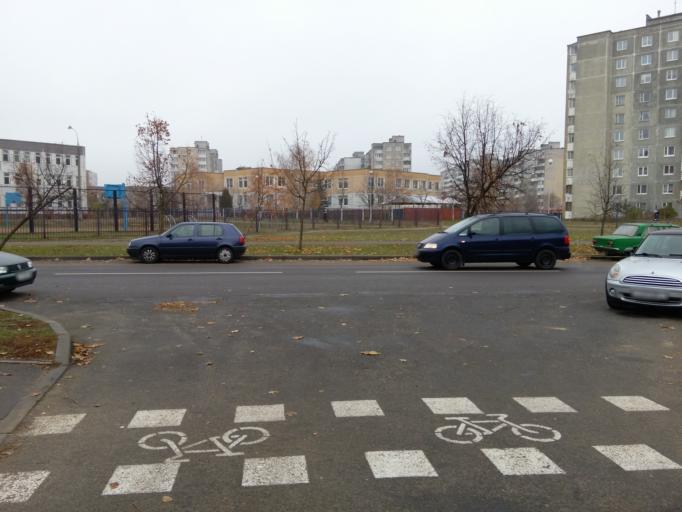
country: BY
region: Minsk
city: Borovlyany
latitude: 53.9504
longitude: 27.6884
